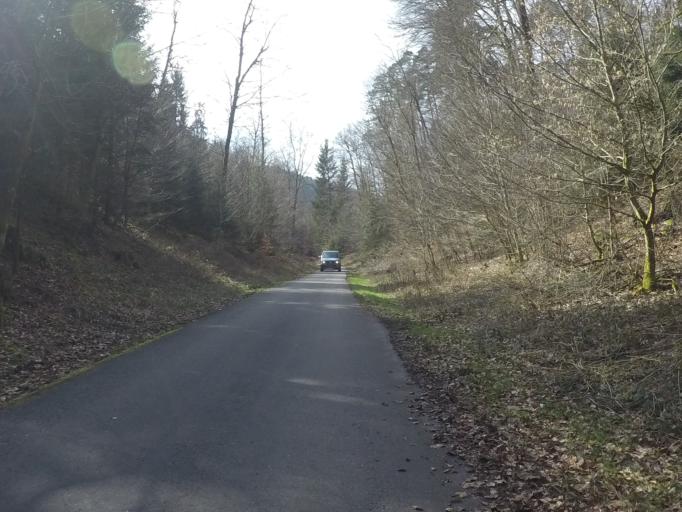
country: DE
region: Rheinland-Pfalz
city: Munchweiler an der Rodalbe
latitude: 49.2117
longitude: 7.7268
